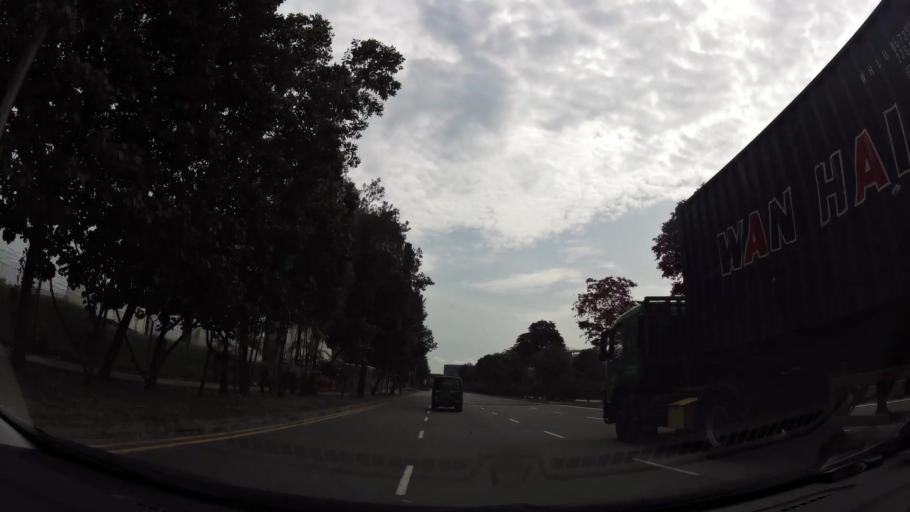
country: SG
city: Singapore
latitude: 1.3144
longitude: 103.7136
